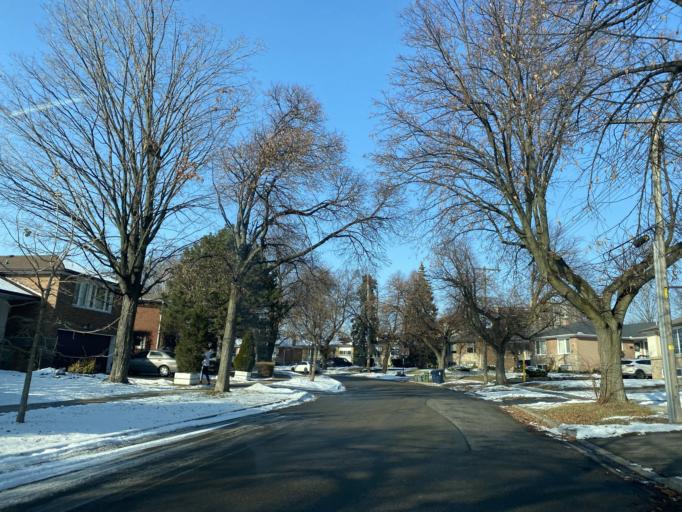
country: CA
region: Ontario
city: Etobicoke
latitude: 43.6720
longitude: -79.5654
